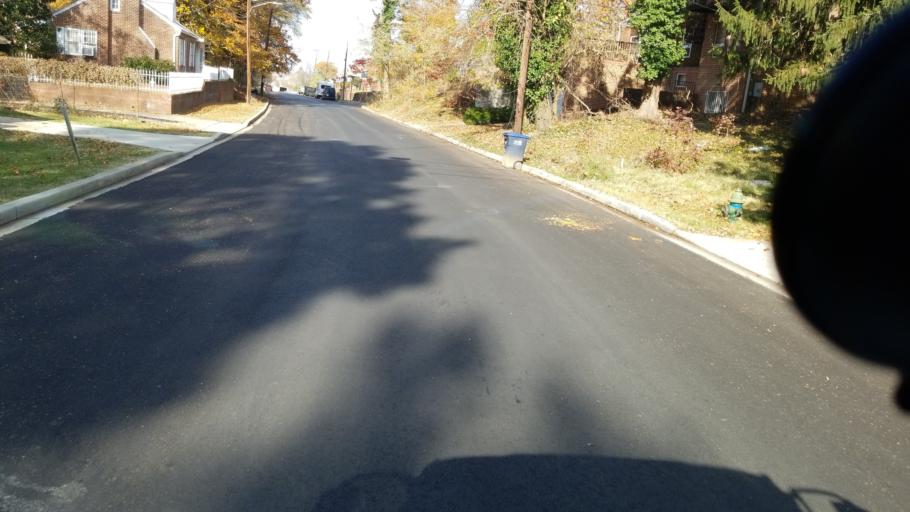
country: US
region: Maryland
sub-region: Prince George's County
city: Coral Hills
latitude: 38.8754
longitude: -76.9389
